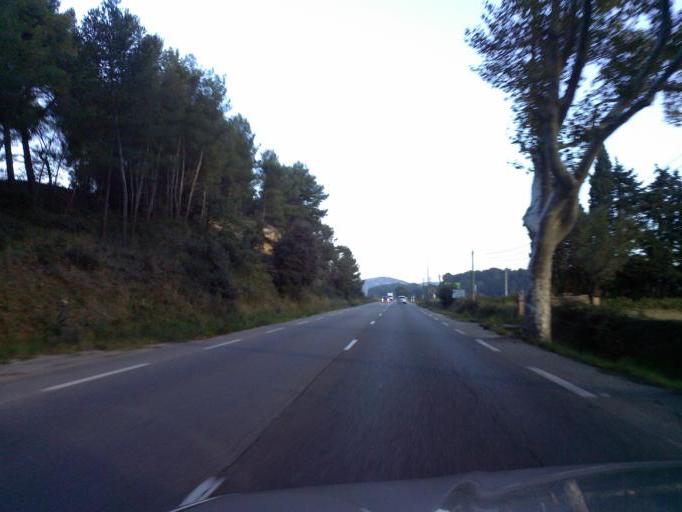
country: FR
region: Provence-Alpes-Cote d'Azur
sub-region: Departement des Bouches-du-Rhone
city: Lambesc
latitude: 43.6635
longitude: 5.2516
